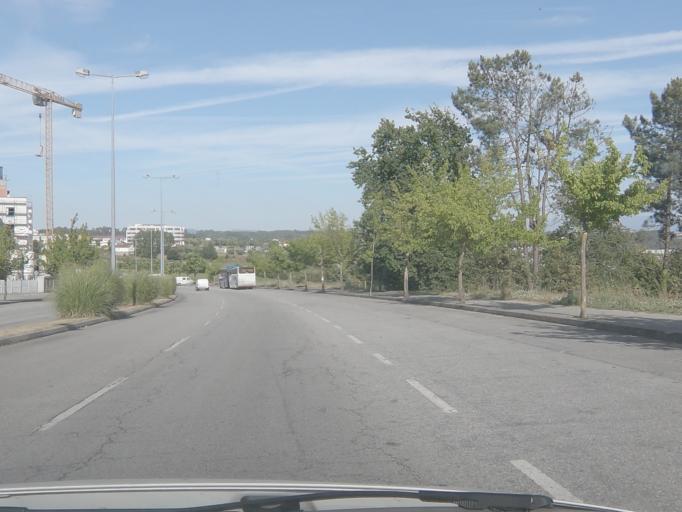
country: PT
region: Viseu
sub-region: Viseu
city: Viseu
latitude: 40.6410
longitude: -7.9169
